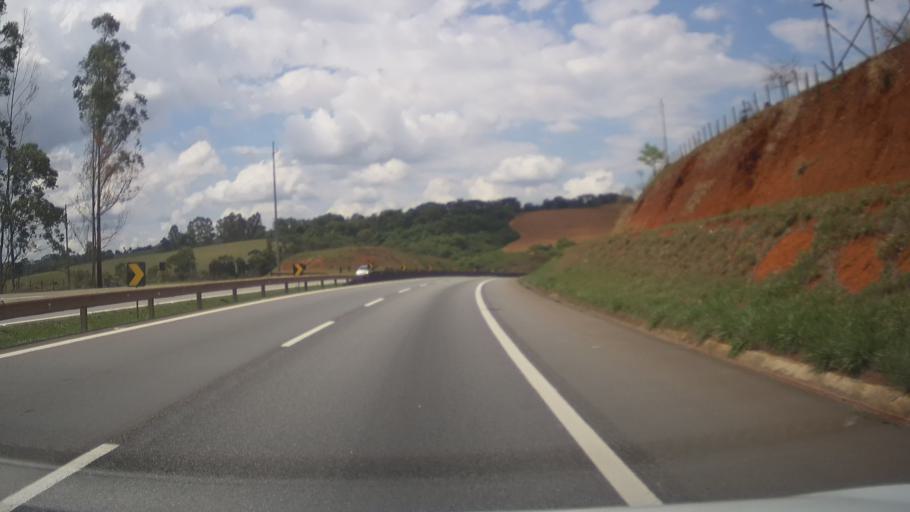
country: BR
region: Minas Gerais
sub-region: Nepomuceno
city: Nepomuceno
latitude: -21.2903
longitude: -45.1477
